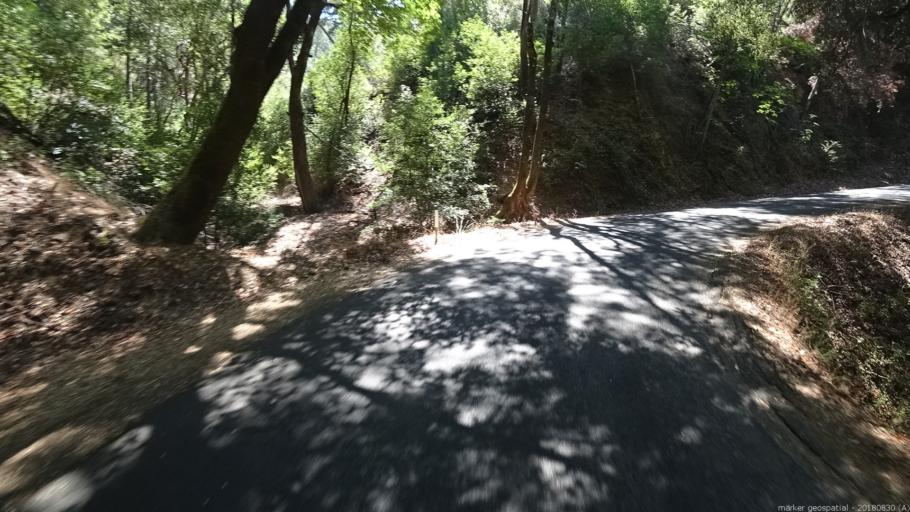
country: US
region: California
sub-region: Monterey County
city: Greenfield
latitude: 36.0128
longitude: -121.4314
